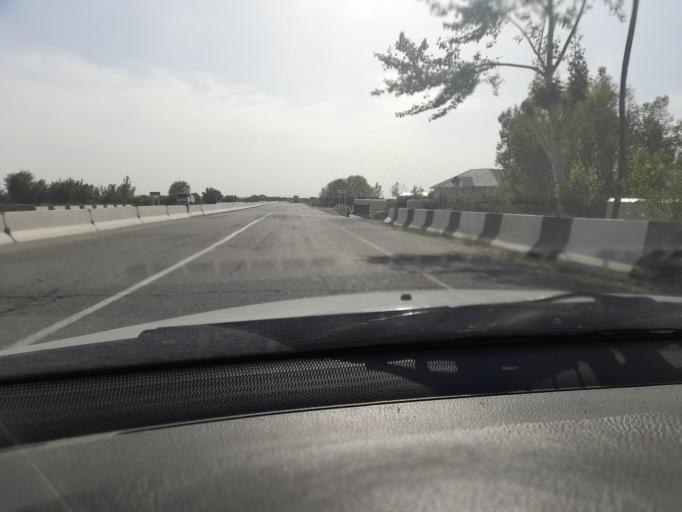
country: UZ
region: Samarqand
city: Ishtixon
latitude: 39.9347
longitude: 66.3727
